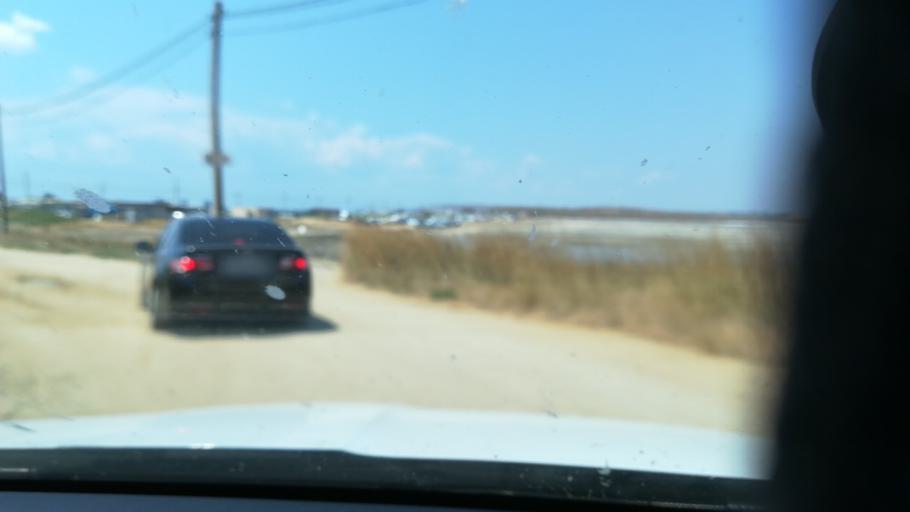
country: RU
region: Krasnodarskiy
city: Vyshestebliyevskaya
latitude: 45.1125
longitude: 36.8737
